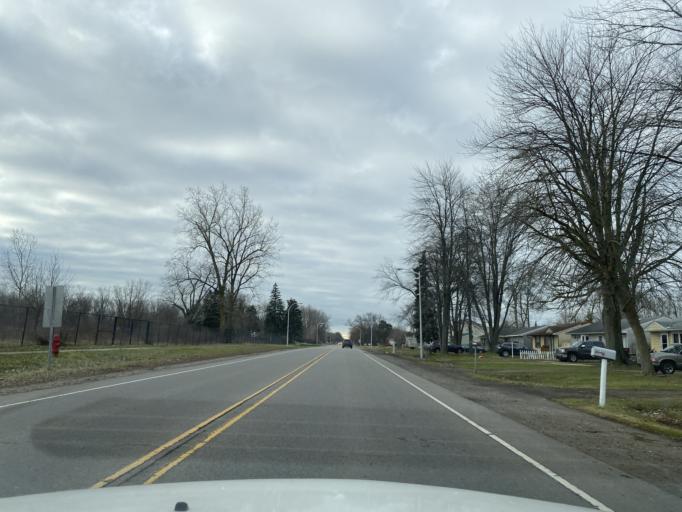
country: US
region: Michigan
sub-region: Wayne County
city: Taylor
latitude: 42.2033
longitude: -83.2874
